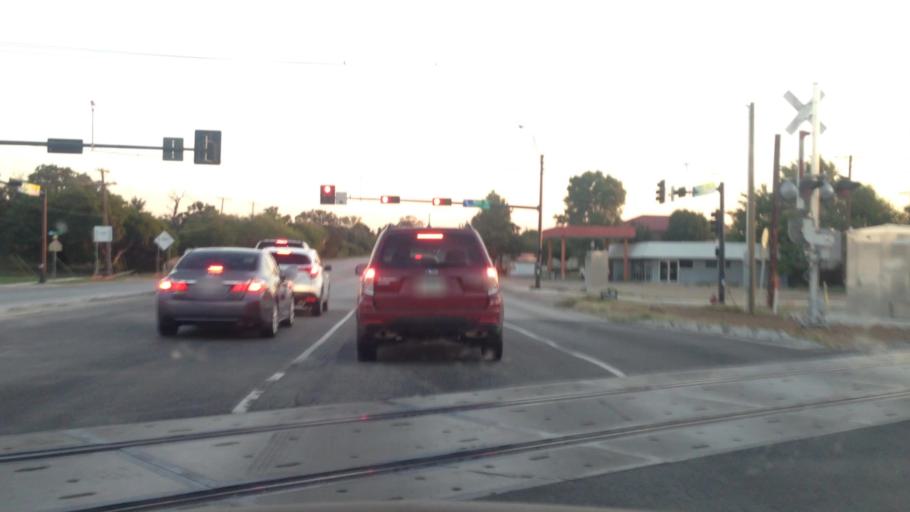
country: US
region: Texas
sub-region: Tarrant County
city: North Richland Hills
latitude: 32.8667
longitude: -97.2086
